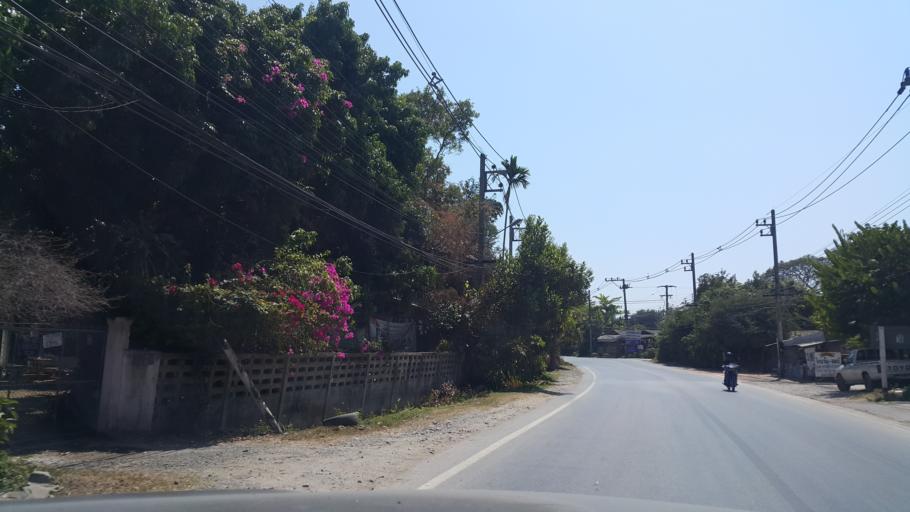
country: TH
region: Chiang Mai
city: San Sai
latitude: 18.8706
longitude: 99.0509
